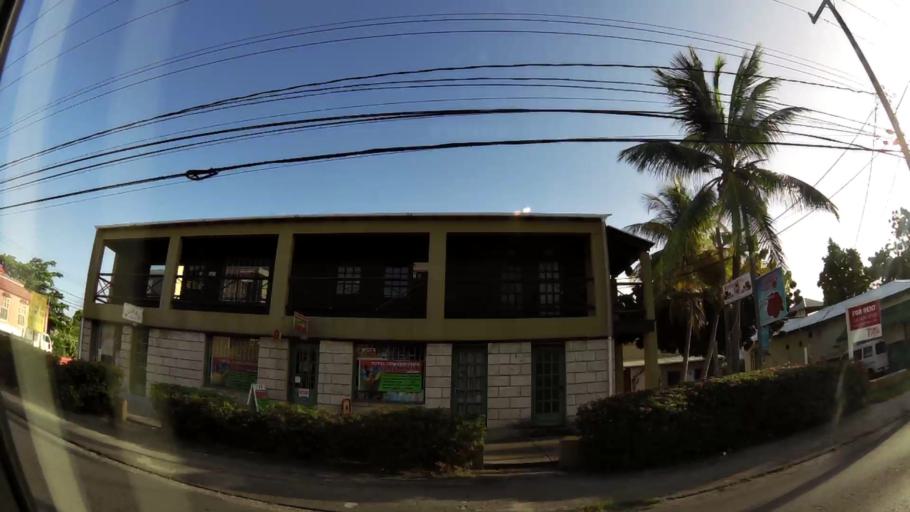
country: BB
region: Saint Michael
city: Bridgetown
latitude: 13.0769
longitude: -59.6027
